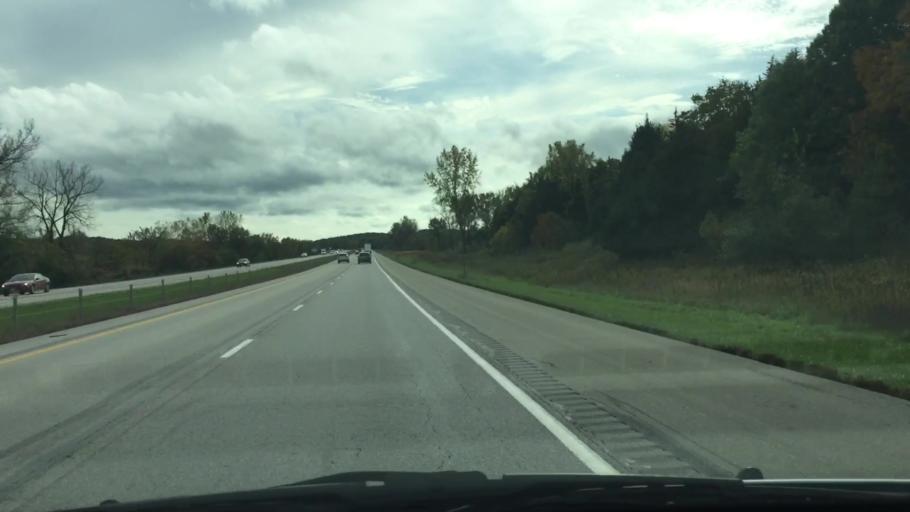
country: US
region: Iowa
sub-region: Clarke County
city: Osceola
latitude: 41.0938
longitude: -93.7790
